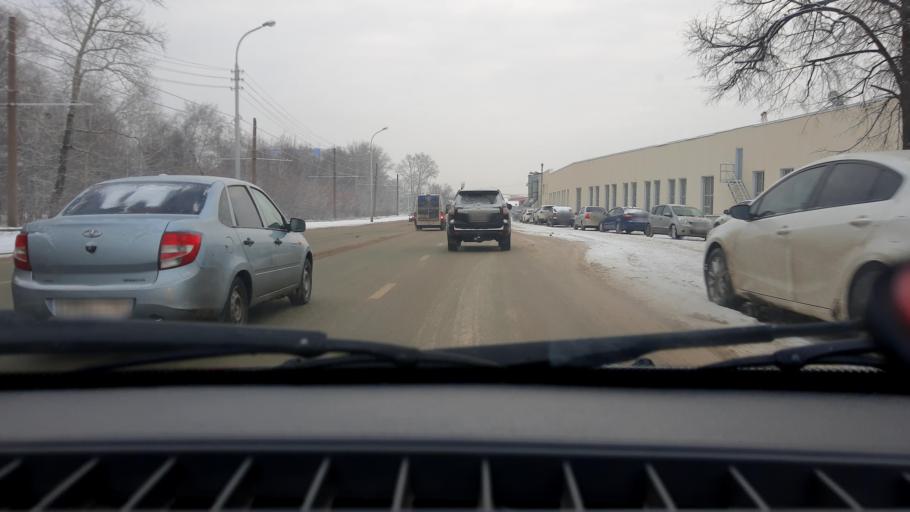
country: RU
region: Bashkortostan
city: Ufa
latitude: 54.7983
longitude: 56.1273
